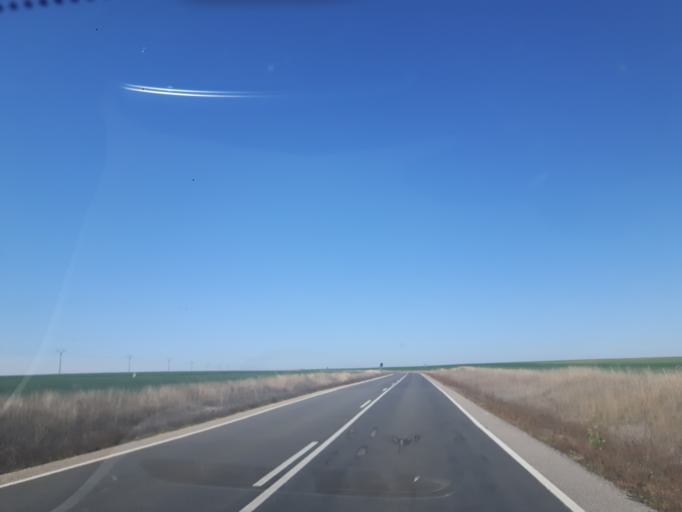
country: ES
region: Castille and Leon
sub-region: Provincia de Salamanca
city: Nava de Sotrobal
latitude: 40.8865
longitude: -5.3022
